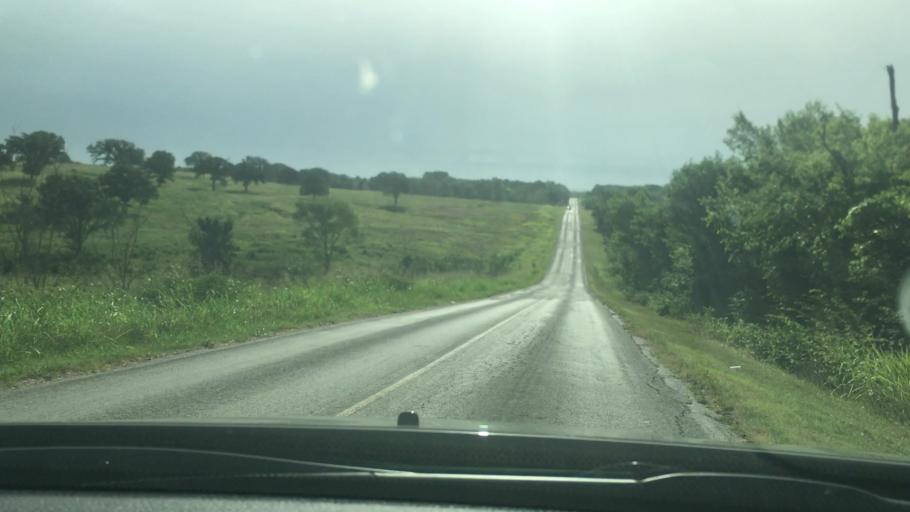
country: US
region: Oklahoma
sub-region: Pontotoc County
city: Byng
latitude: 34.8737
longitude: -96.5894
